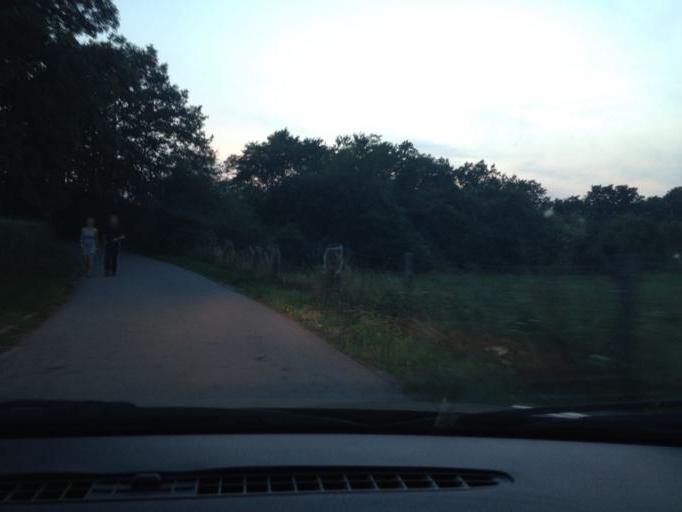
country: DE
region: Saarland
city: Namborn
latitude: 49.5467
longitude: 7.1358
